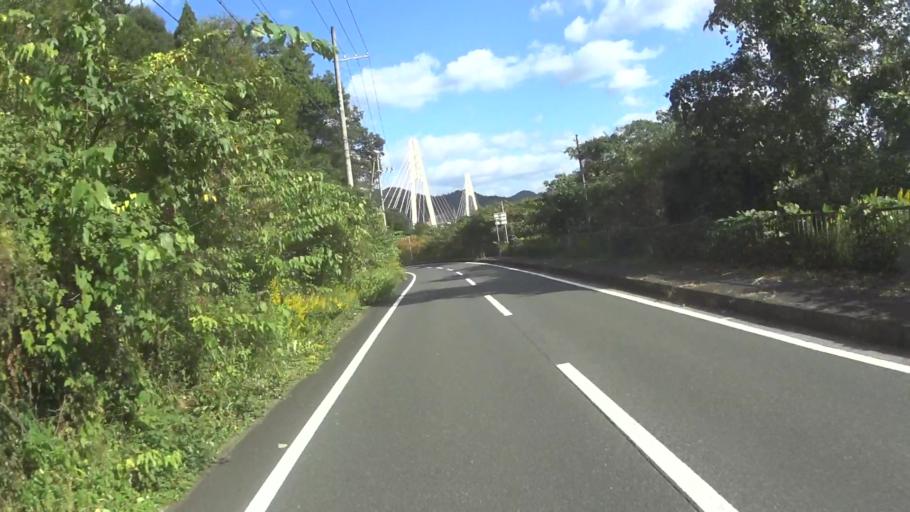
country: JP
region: Kyoto
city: Maizuru
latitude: 35.5113
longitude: 135.3813
